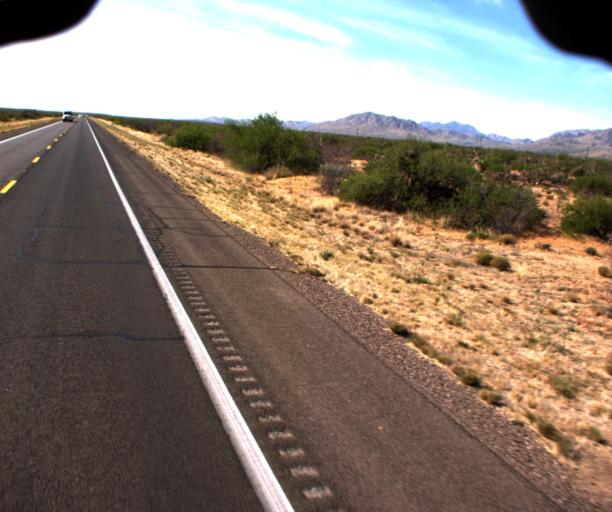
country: US
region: Arizona
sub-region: Graham County
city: Swift Trail Junction
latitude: 32.6699
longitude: -109.7033
